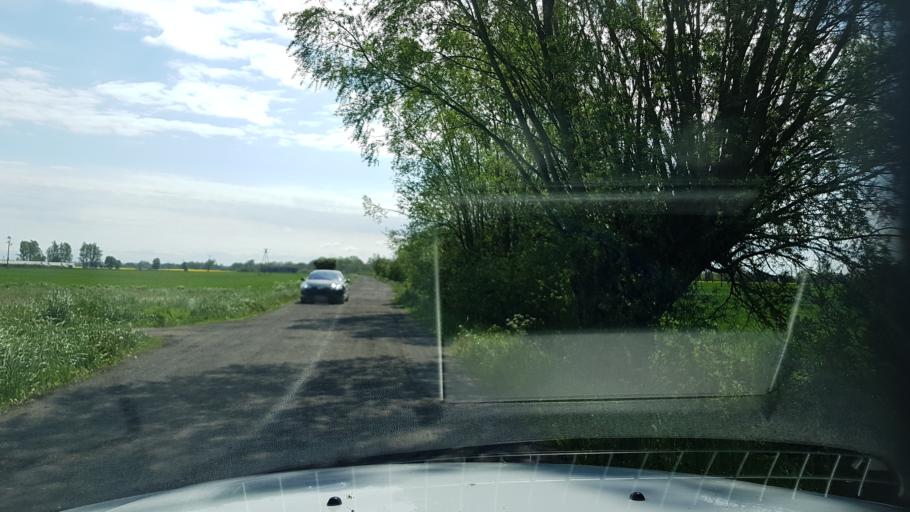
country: PL
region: West Pomeranian Voivodeship
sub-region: Powiat kolobrzeski
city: Ustronie Morskie
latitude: 54.2161
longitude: 15.8358
